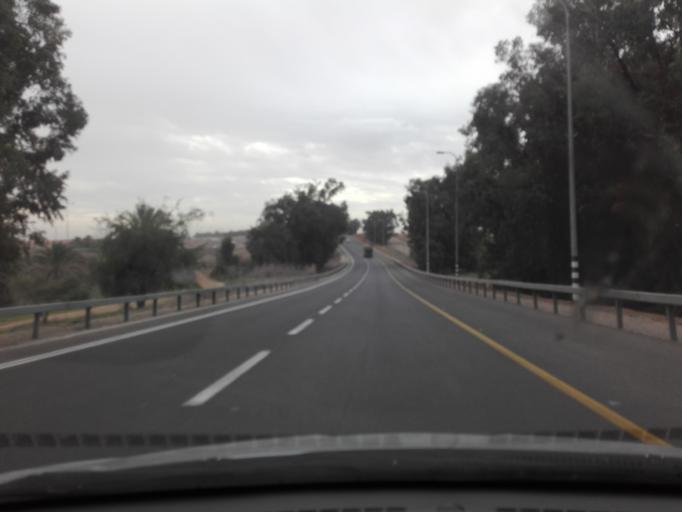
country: IL
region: Southern District
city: Lehavim
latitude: 31.4875
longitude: 34.7776
